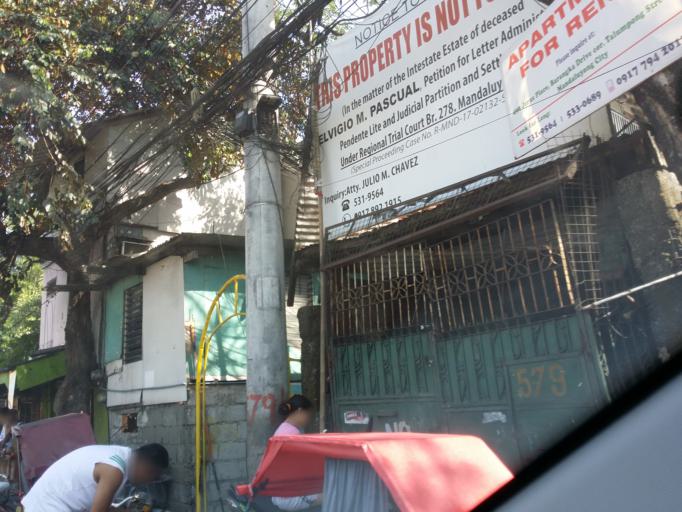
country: PH
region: Metro Manila
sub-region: Mandaluyong
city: Mandaluyong City
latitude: 14.5743
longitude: 121.0268
